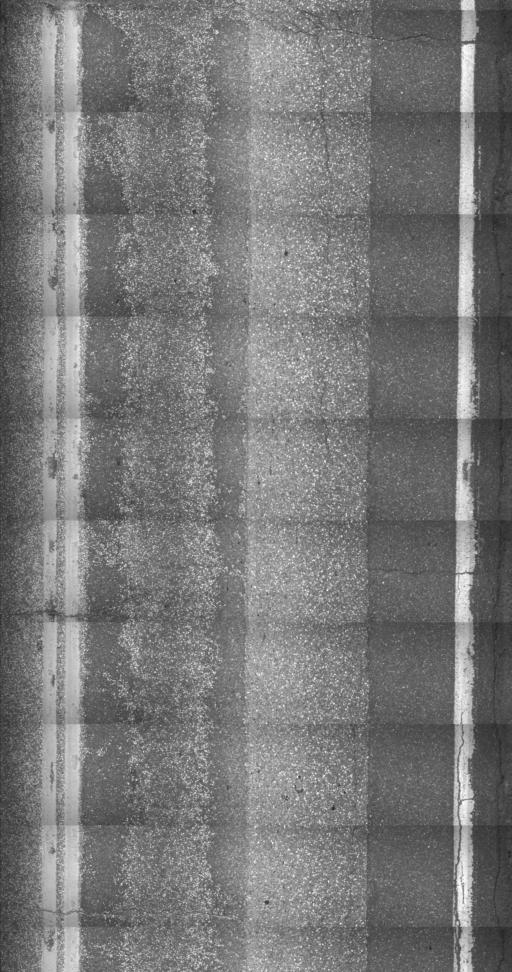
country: US
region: Vermont
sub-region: Washington County
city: Waterbury
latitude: 44.3250
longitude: -72.7441
